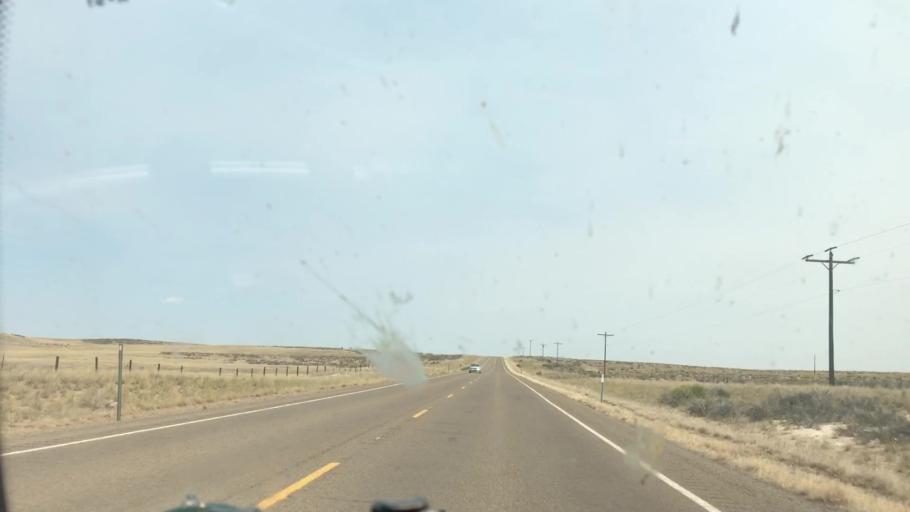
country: US
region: Idaho
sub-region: Owyhee County
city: Homedale
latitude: 42.8561
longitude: -117.5763
